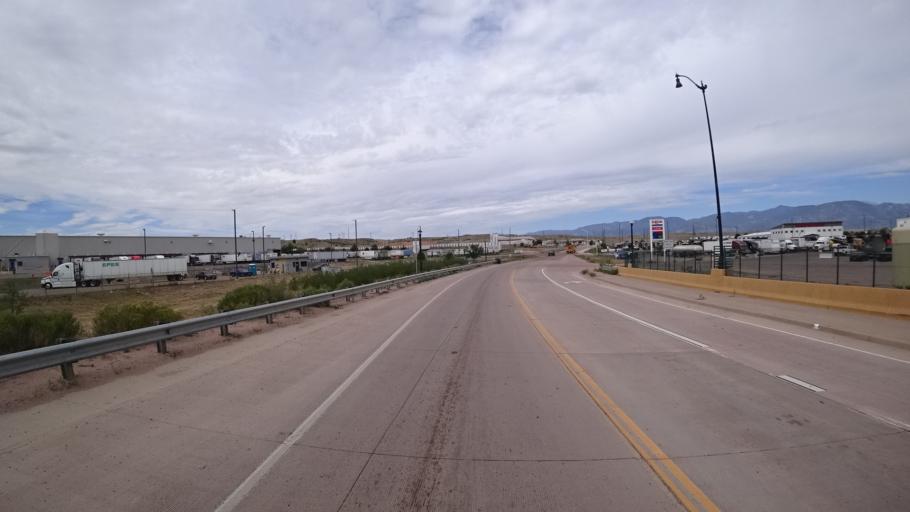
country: US
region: Colorado
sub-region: El Paso County
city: Fountain
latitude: 38.6717
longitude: -104.7115
